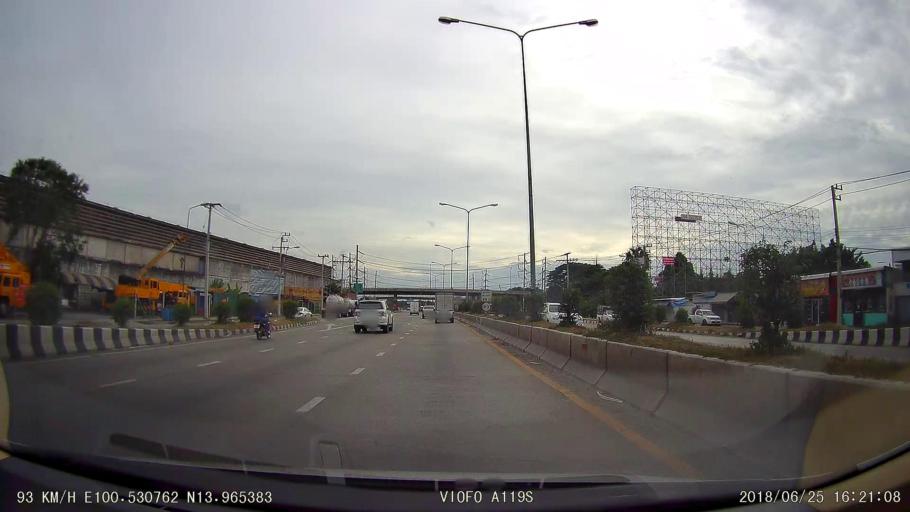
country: TH
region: Phra Nakhon Si Ayutthaya
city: Ban Bang Kadi Pathum Thani
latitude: 13.9652
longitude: 100.5309
